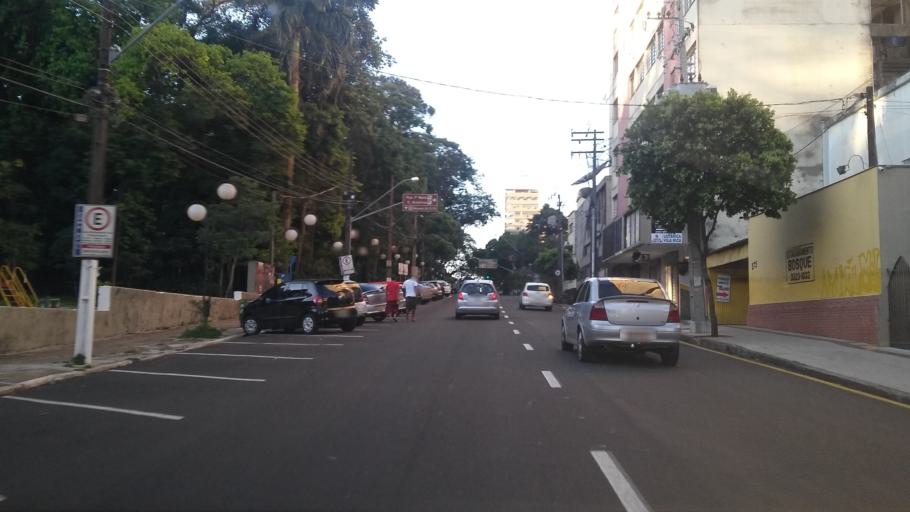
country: BR
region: Parana
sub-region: Londrina
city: Londrina
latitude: -23.3141
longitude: -51.1589
